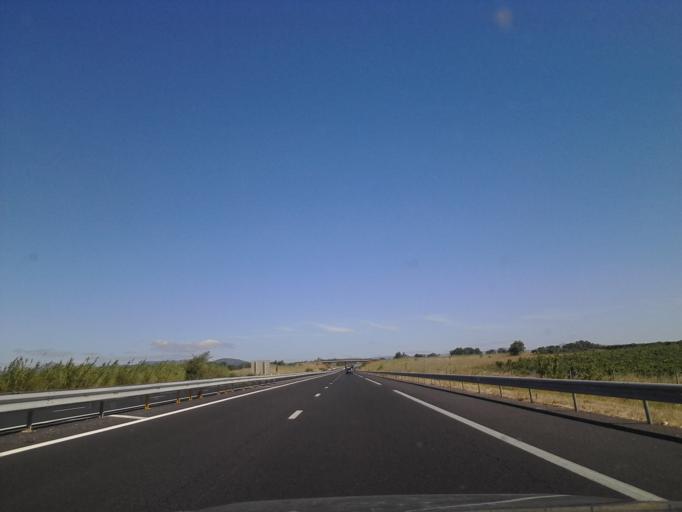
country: FR
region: Languedoc-Roussillon
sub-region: Departement de l'Herault
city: Lezignan-la-Cebe
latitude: 43.5021
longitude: 3.4449
